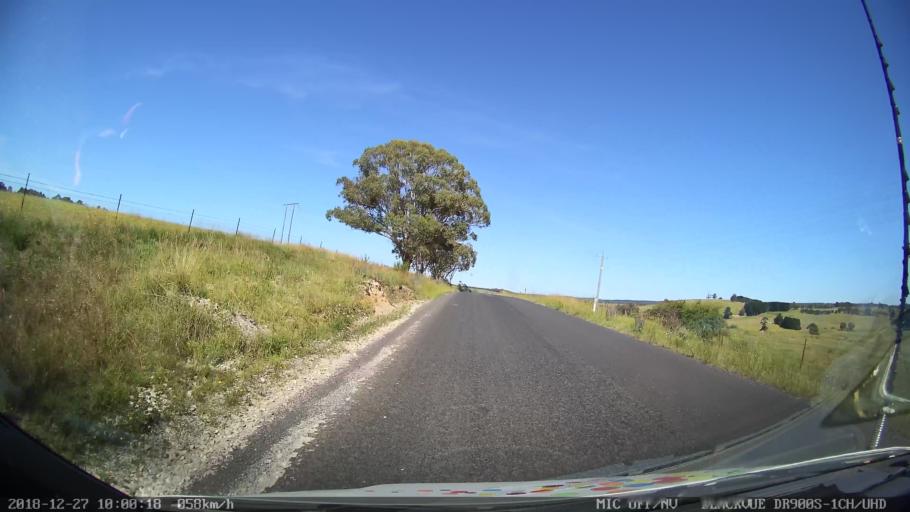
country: AU
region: New South Wales
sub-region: Lithgow
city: Portland
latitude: -33.4371
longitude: 149.9430
